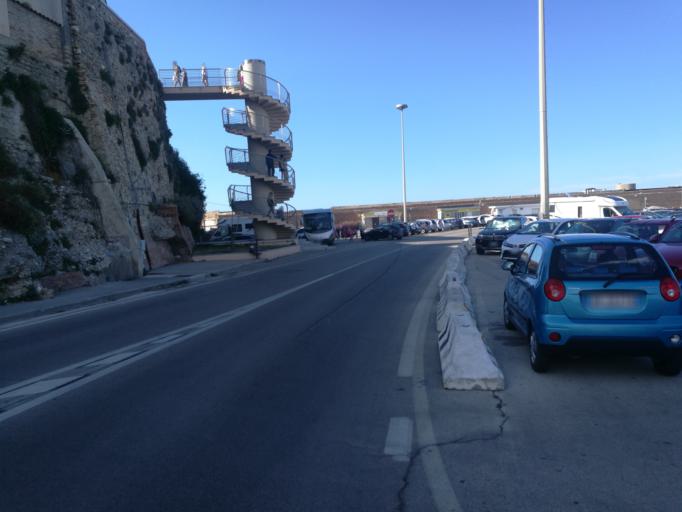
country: IT
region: Molise
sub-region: Provincia di Campobasso
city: Termoli
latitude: 42.0045
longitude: 14.9986
